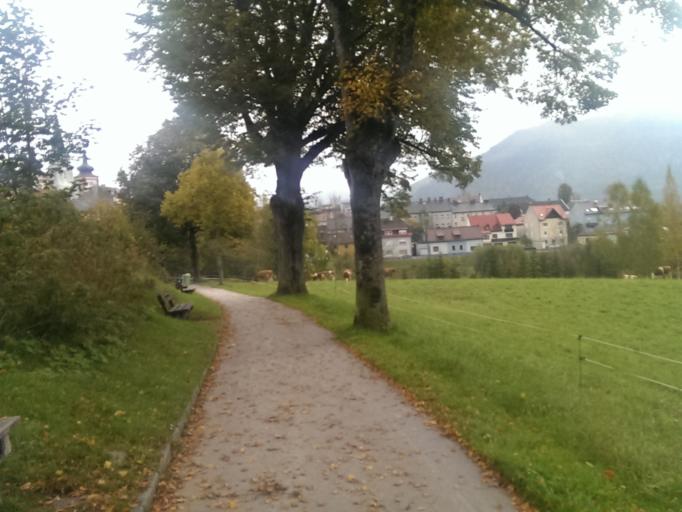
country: AT
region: Styria
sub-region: Politischer Bezirk Bruck-Muerzzuschlag
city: Mariazell
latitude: 47.7749
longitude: 15.3136
